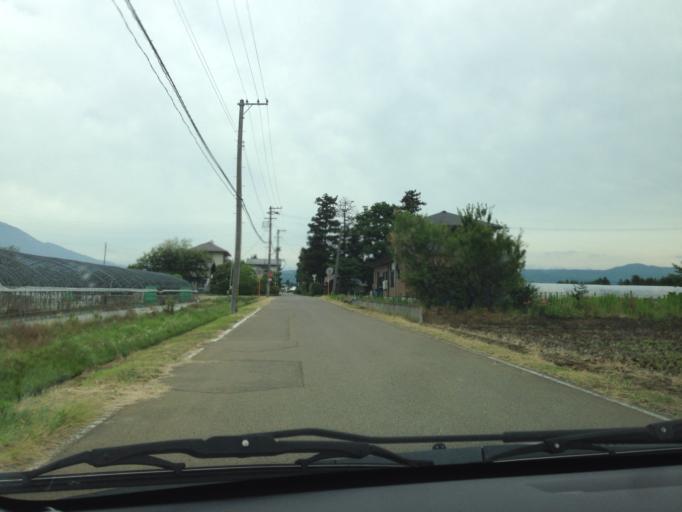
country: JP
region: Fukushima
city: Kitakata
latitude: 37.5369
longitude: 139.8916
